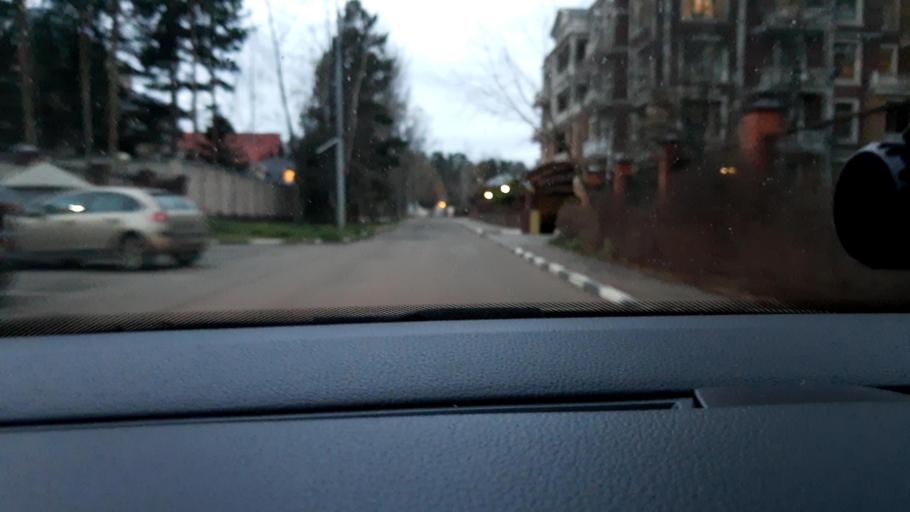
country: RU
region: Moskovskaya
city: Zarech'ye
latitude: 55.6794
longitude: 37.3855
